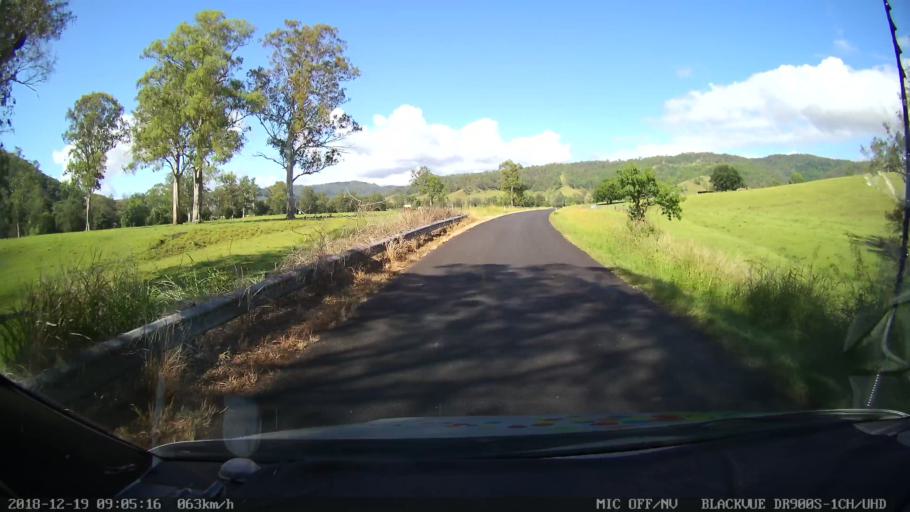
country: AU
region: New South Wales
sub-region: Kyogle
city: Kyogle
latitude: -28.4633
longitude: 152.9448
